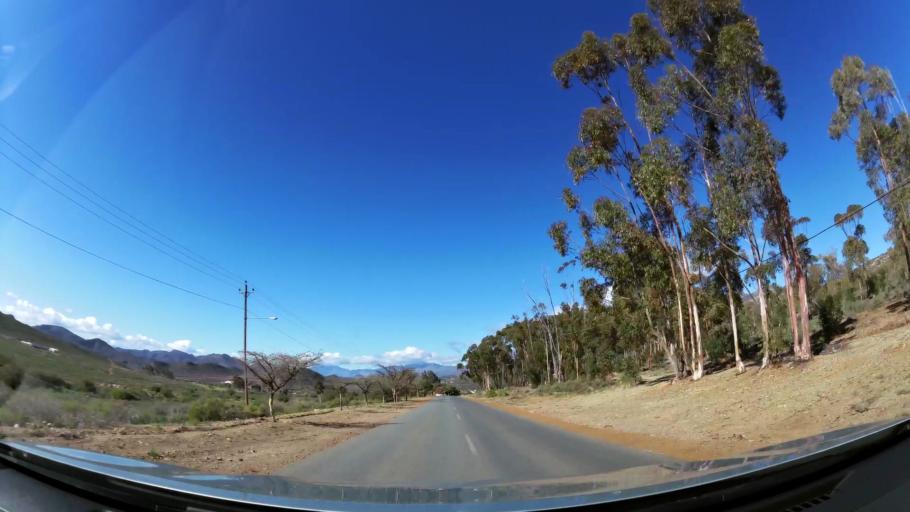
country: ZA
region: Western Cape
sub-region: Cape Winelands District Municipality
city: Ashton
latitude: -33.7684
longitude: 20.1291
